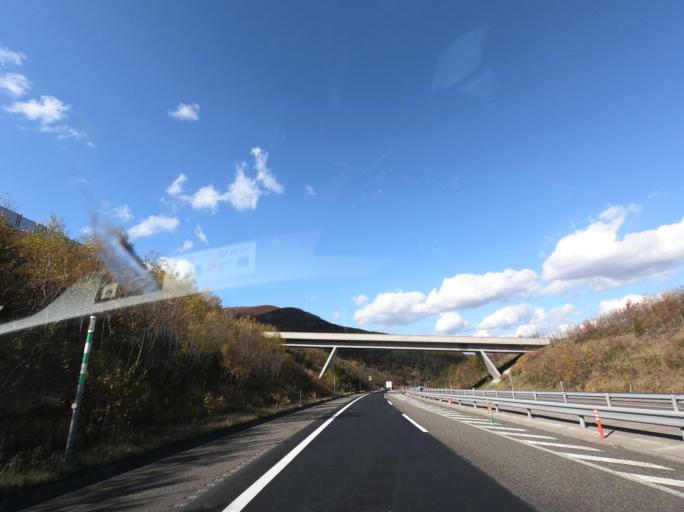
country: JP
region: Hokkaido
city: Otofuke
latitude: 43.0397
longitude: 142.7843
